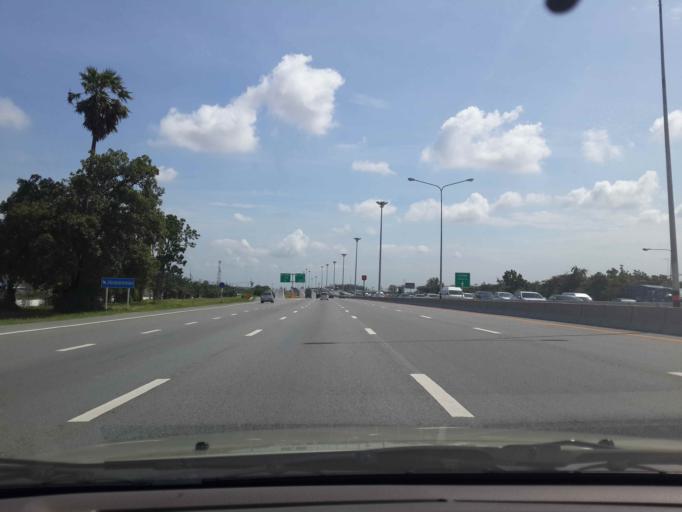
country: TH
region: Chon Buri
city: Chon Buri
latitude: 13.3970
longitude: 101.0472
